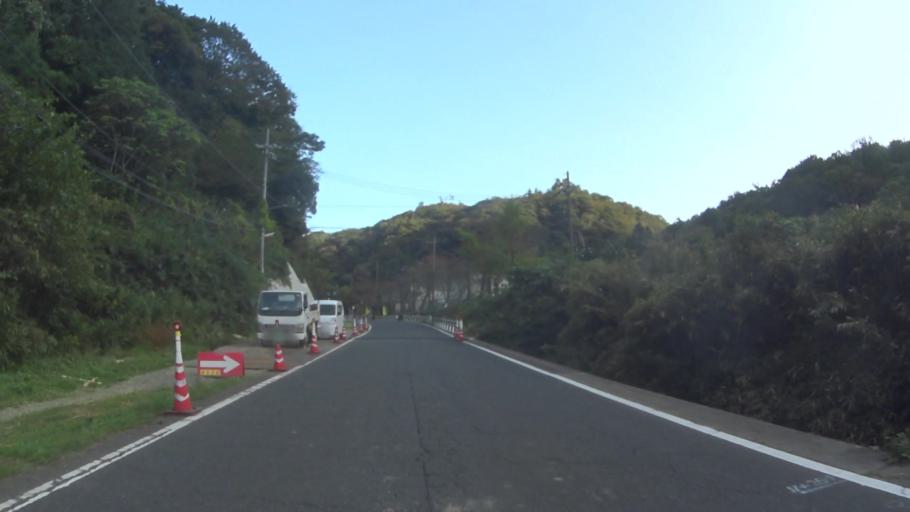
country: JP
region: Kyoto
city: Miyazu
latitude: 35.6886
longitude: 135.2801
